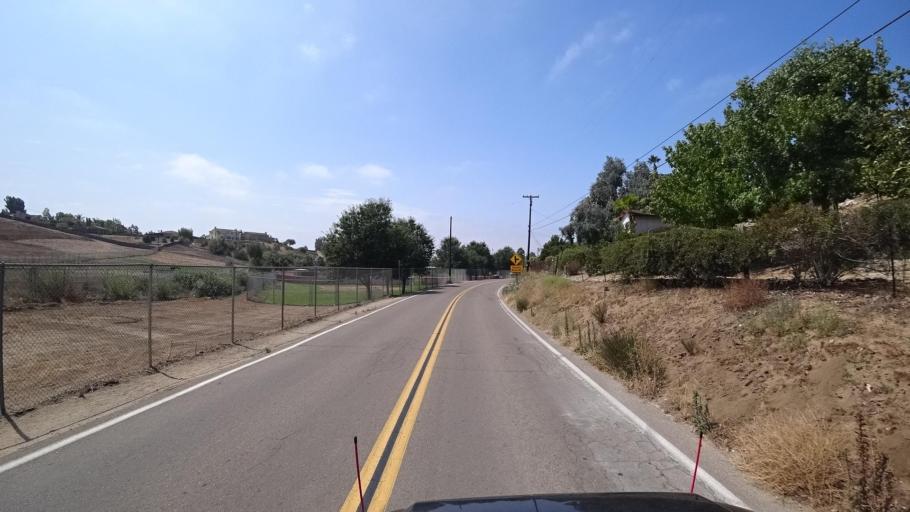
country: US
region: California
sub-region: San Diego County
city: Fallbrook
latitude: 33.3529
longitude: -117.2357
